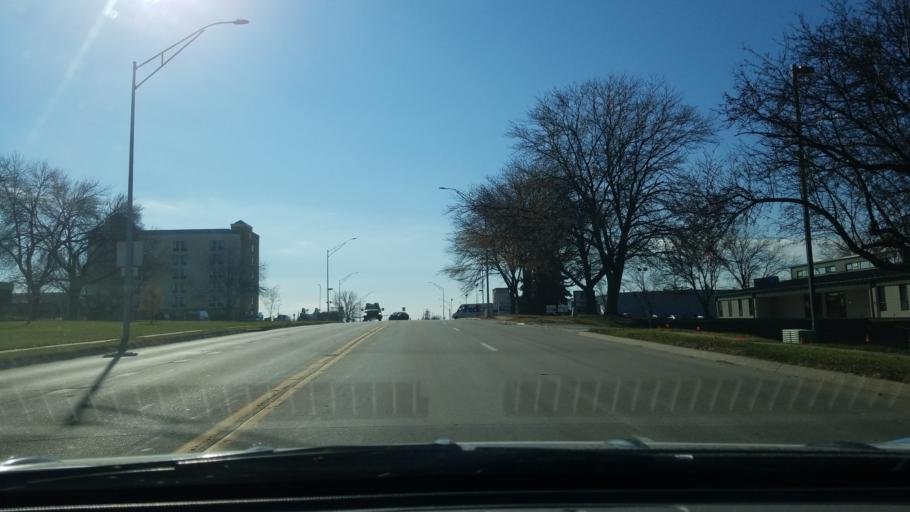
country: US
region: Nebraska
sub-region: Douglas County
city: Ralston
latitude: 41.2153
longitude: -96.0816
